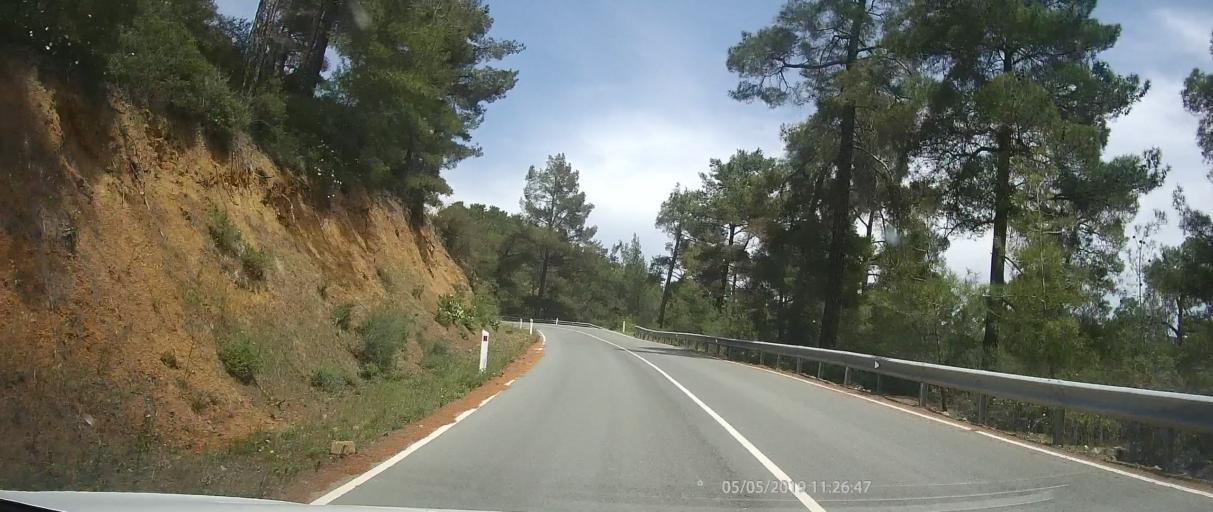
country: CY
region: Limassol
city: Pachna
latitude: 34.9303
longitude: 32.6471
